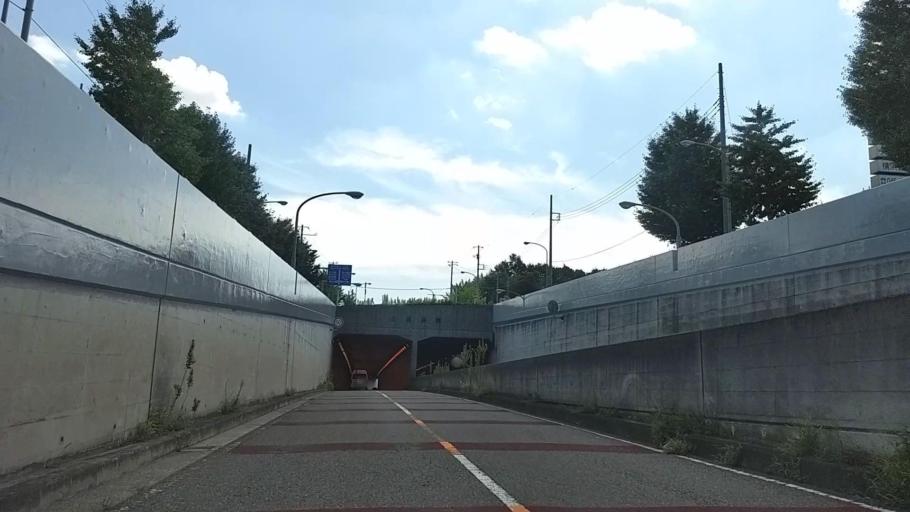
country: JP
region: Kanagawa
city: Yokohama
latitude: 35.5277
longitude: 139.5662
